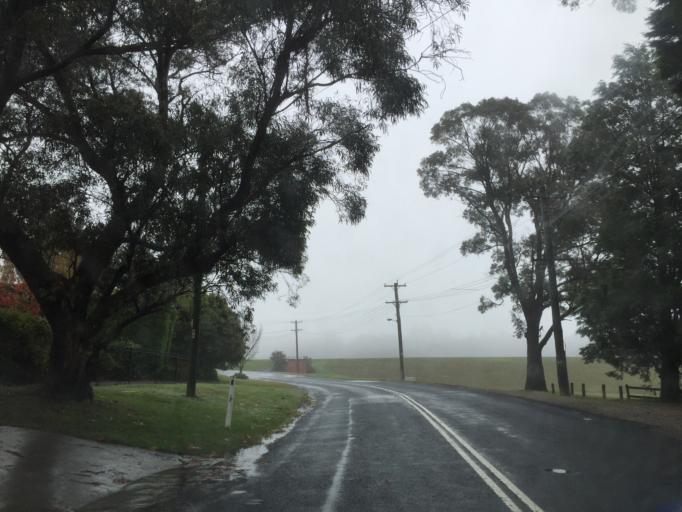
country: AU
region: New South Wales
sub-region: Blue Mountains Municipality
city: Leura
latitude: -33.7053
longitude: 150.3726
